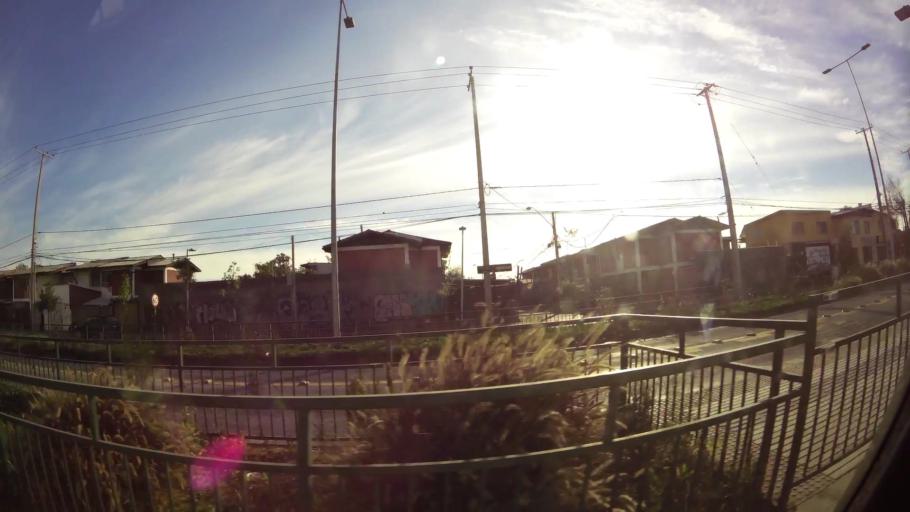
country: CL
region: Santiago Metropolitan
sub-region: Provincia de Santiago
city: Lo Prado
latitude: -33.4526
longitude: -70.7062
